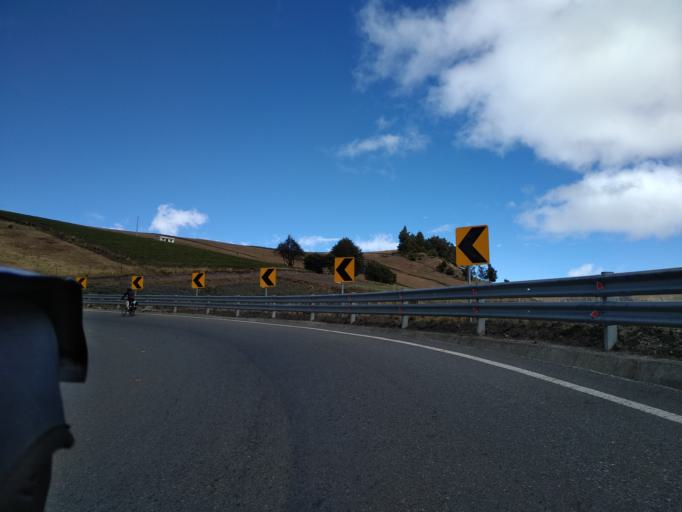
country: EC
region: Cotopaxi
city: Pujili
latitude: -0.9453
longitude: -78.9209
